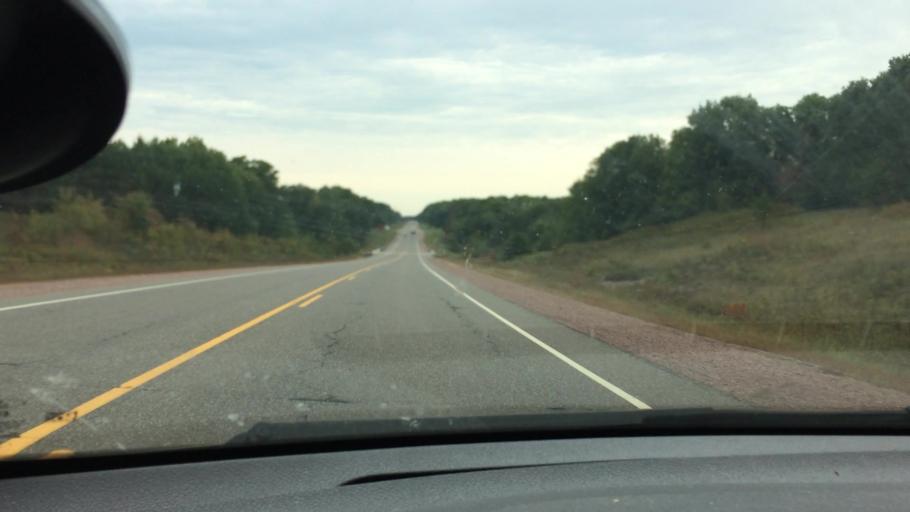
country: US
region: Wisconsin
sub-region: Clark County
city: Neillsville
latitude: 44.5692
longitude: -90.7255
